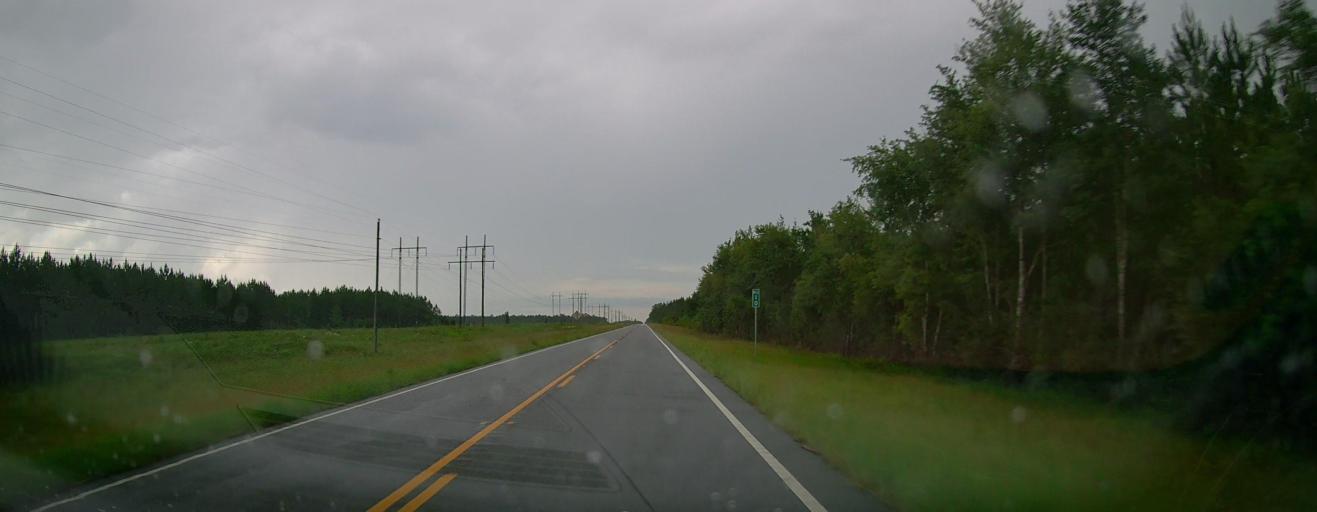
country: US
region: Georgia
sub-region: Brantley County
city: Nahunta
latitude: 31.3371
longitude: -81.8685
